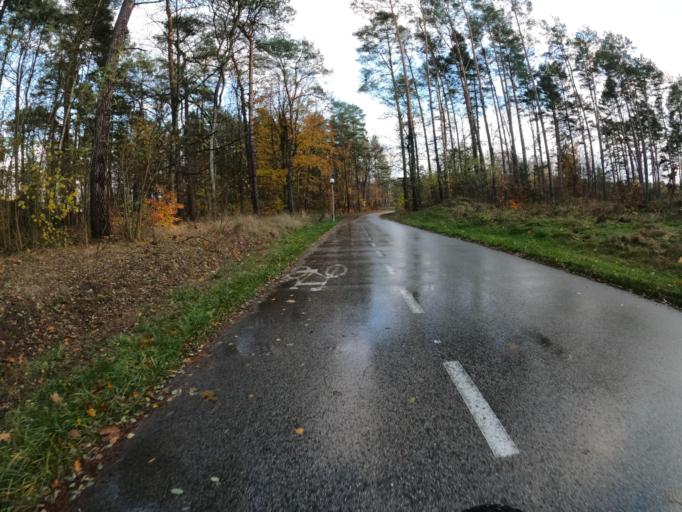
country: PL
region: West Pomeranian Voivodeship
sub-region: Powiat walecki
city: Tuczno
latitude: 53.1891
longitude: 16.1635
